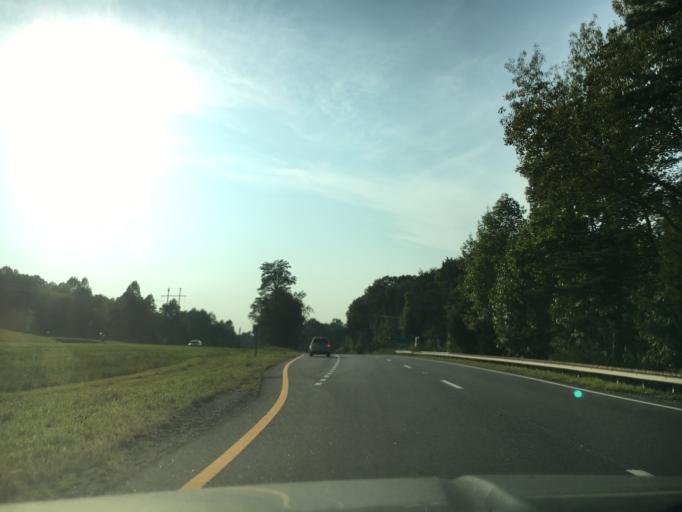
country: US
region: Virginia
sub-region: Prince Edward County
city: Farmville
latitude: 37.2773
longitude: -78.3357
